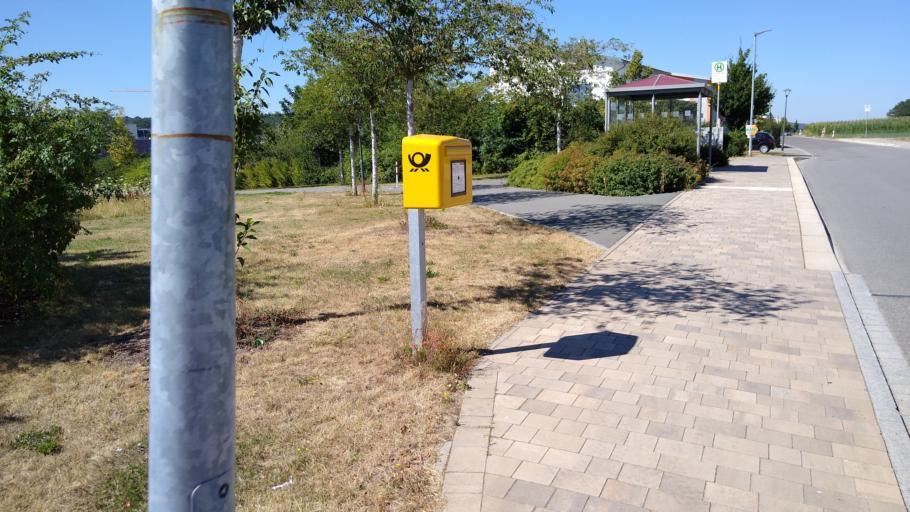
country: DE
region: Bavaria
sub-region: Regierungsbezirk Mittelfranken
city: Seukendorf
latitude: 49.4674
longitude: 10.8858
